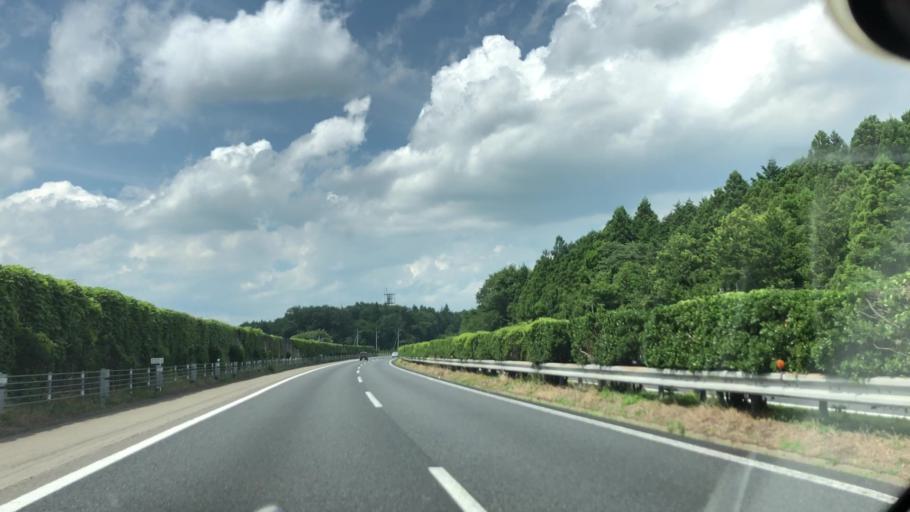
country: JP
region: Tochigi
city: Yaita
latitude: 36.8658
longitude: 139.9124
